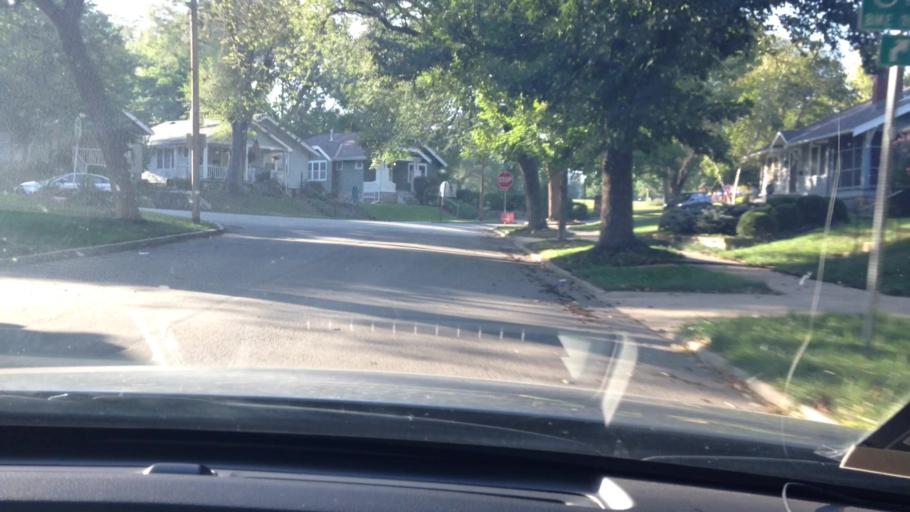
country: US
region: Kansas
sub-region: Johnson County
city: Westwood
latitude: 39.0401
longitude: -94.6049
